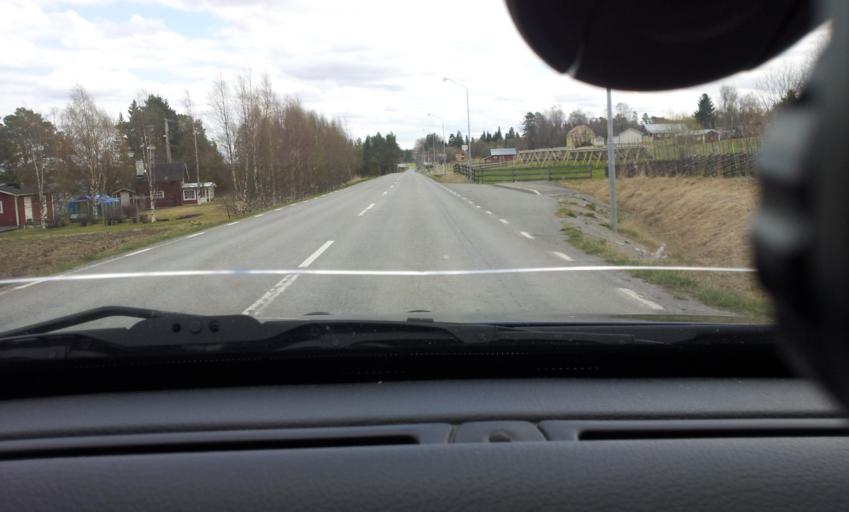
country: SE
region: Jaemtland
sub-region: OEstersunds Kommun
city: Ostersund
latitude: 63.1357
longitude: 14.6407
